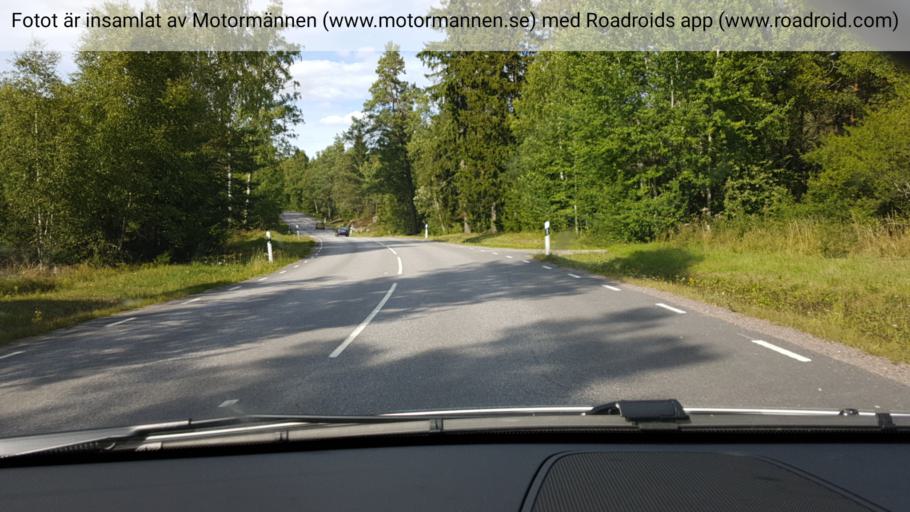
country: SE
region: Stockholm
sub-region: Sodertalje Kommun
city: Pershagen
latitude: 59.1243
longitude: 17.6550
